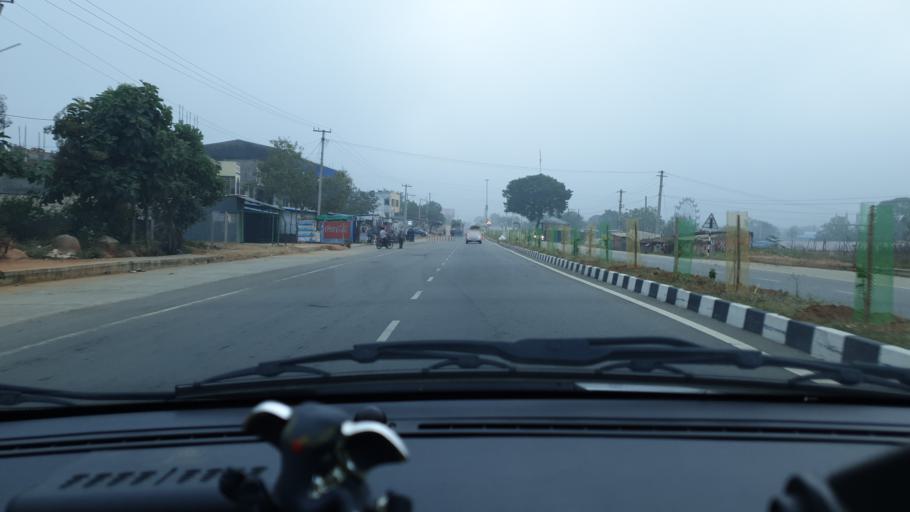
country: IN
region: Telangana
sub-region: Mahbubnagar
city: Farrukhnagar
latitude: 16.9552
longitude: 78.5161
